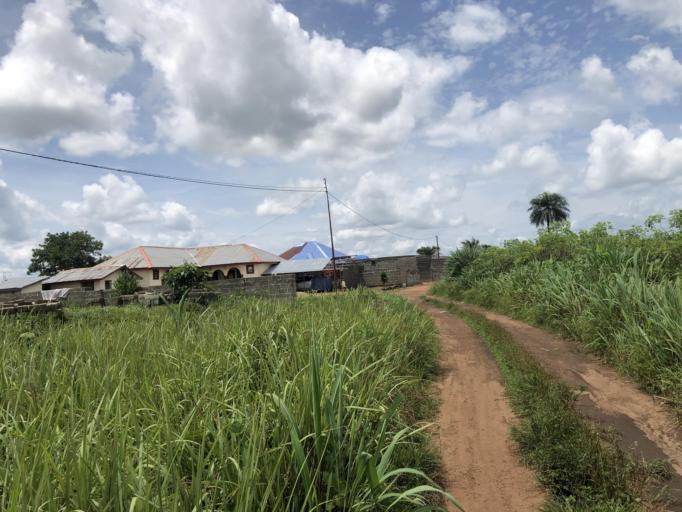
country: SL
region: Northern Province
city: Magburaka
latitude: 8.7035
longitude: -11.9247
